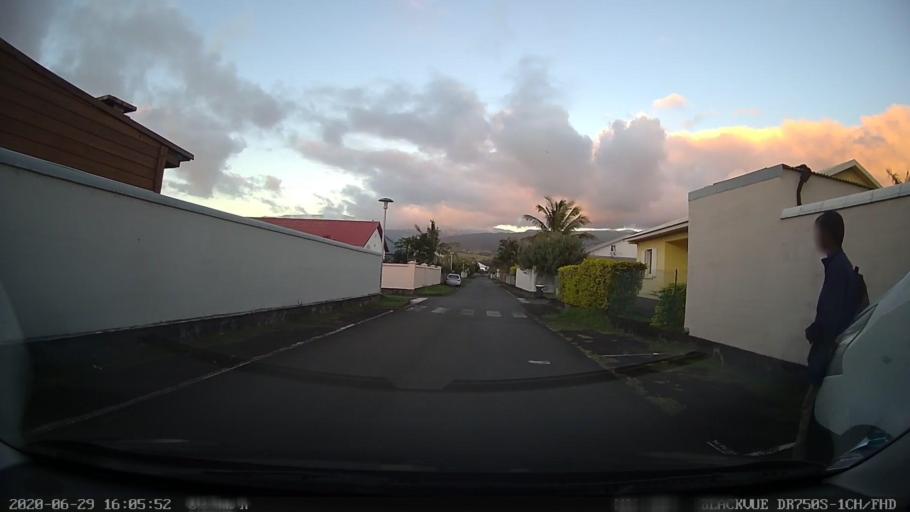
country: RE
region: Reunion
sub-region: Reunion
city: Bras-Panon
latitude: -20.9930
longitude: 55.6826
